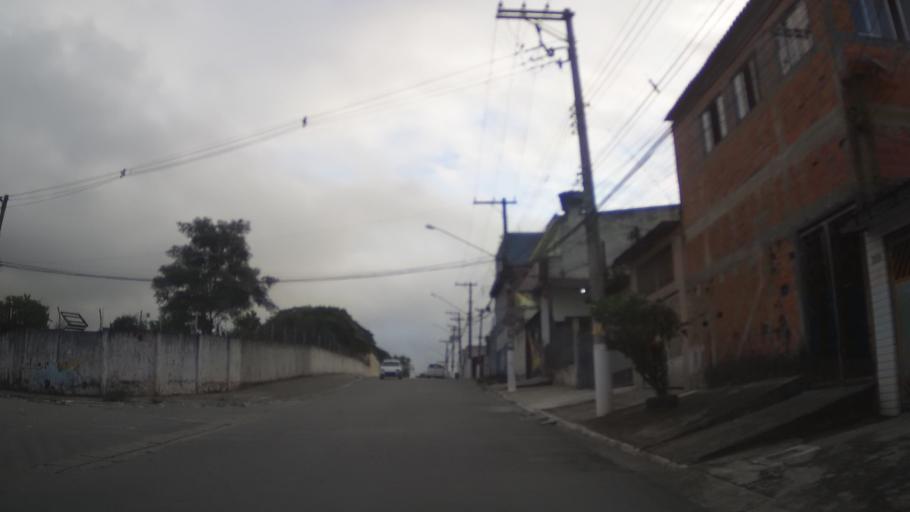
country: BR
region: Sao Paulo
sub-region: Itaquaquecetuba
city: Itaquaquecetuba
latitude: -23.4432
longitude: -46.4268
